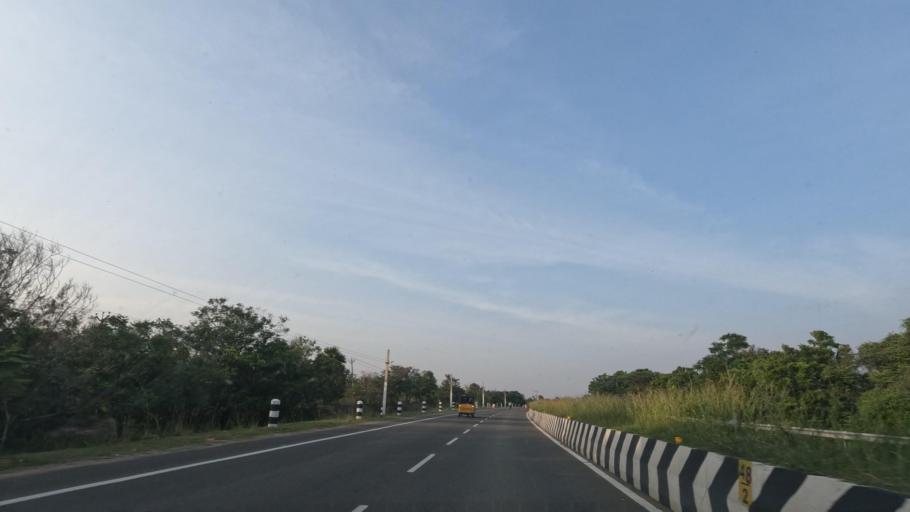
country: IN
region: Tamil Nadu
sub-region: Kancheepuram
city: Mamallapuram
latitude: 12.6736
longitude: 80.2117
